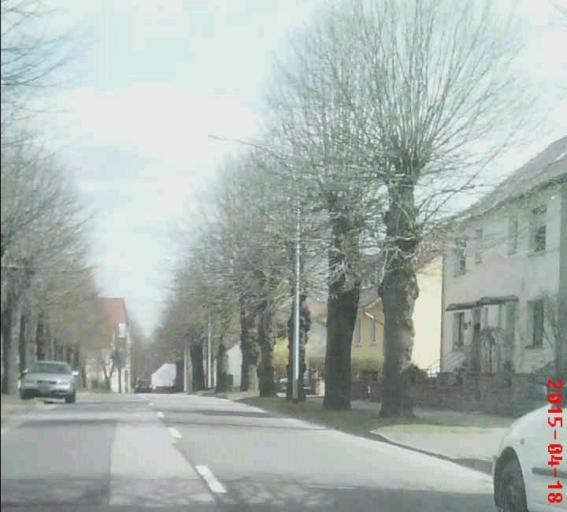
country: DE
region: Thuringia
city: Worbis
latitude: 51.4258
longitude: 10.3544
